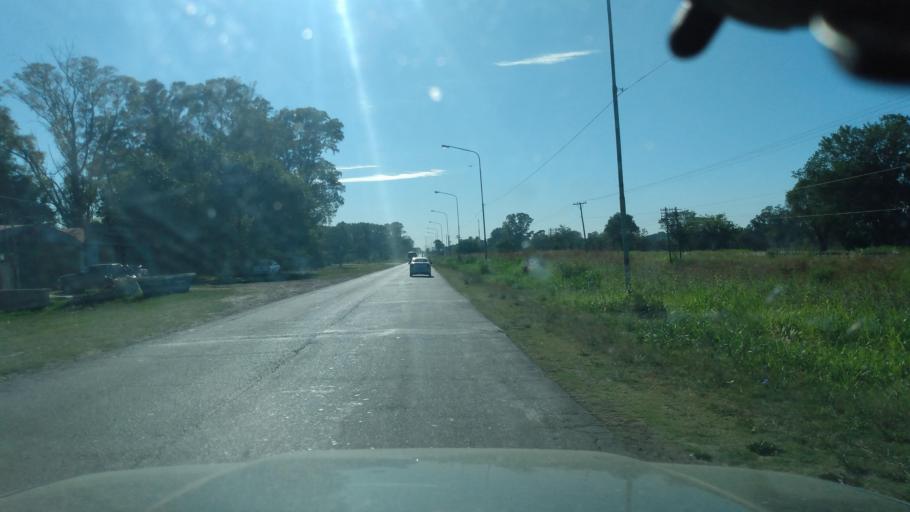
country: AR
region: Buenos Aires
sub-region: Partido de Lujan
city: Lujan
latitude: -34.5816
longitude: -59.0678
